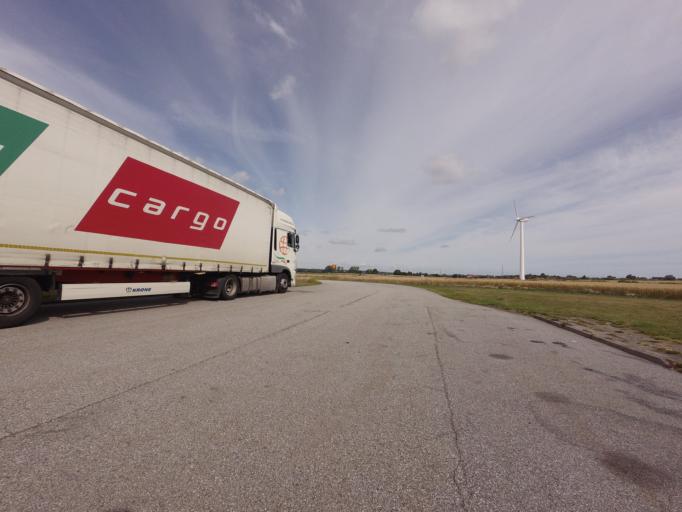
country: SE
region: Skane
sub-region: Simrishamns Kommun
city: Simrishamn
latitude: 55.5352
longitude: 14.3403
